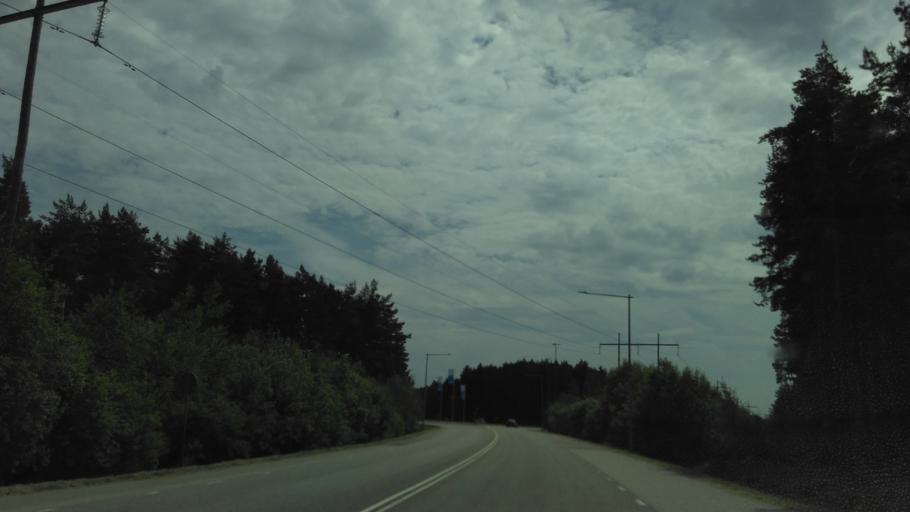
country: SE
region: Vaestra Goetaland
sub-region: Lidkopings Kommun
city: Lidkoping
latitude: 58.4904
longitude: 13.1840
